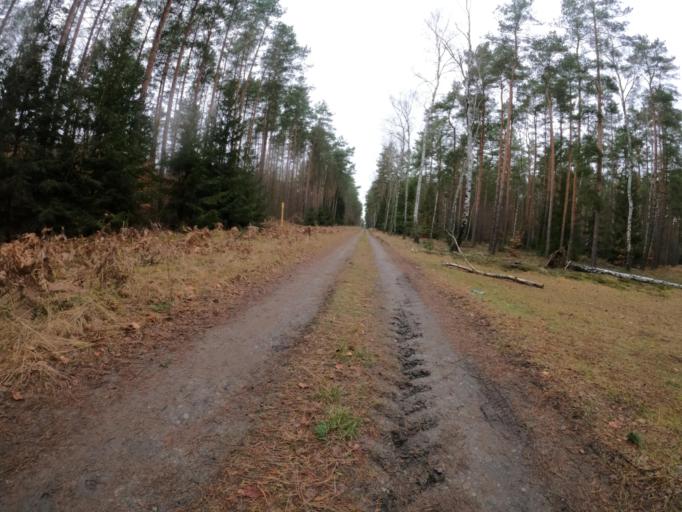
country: PL
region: West Pomeranian Voivodeship
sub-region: Powiat mysliborski
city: Debno
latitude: 52.7535
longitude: 14.7751
